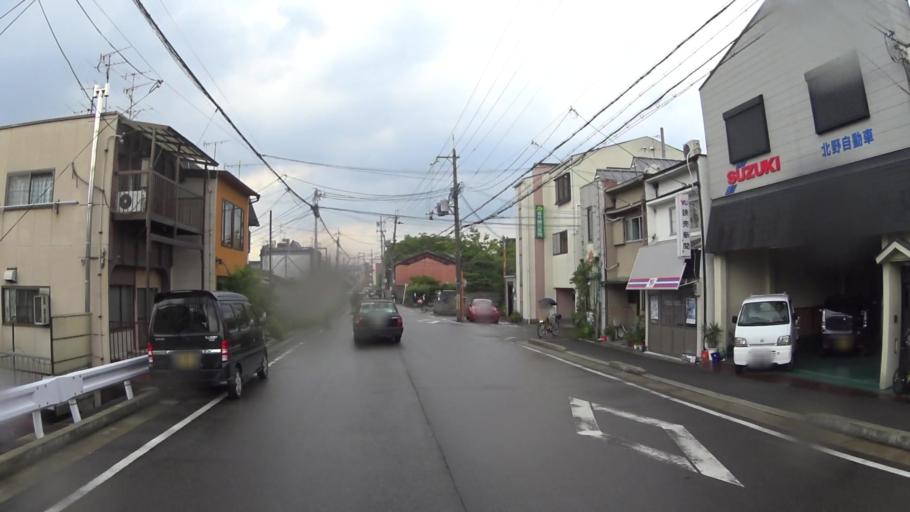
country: JP
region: Kyoto
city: Kyoto
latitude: 35.0258
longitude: 135.7233
